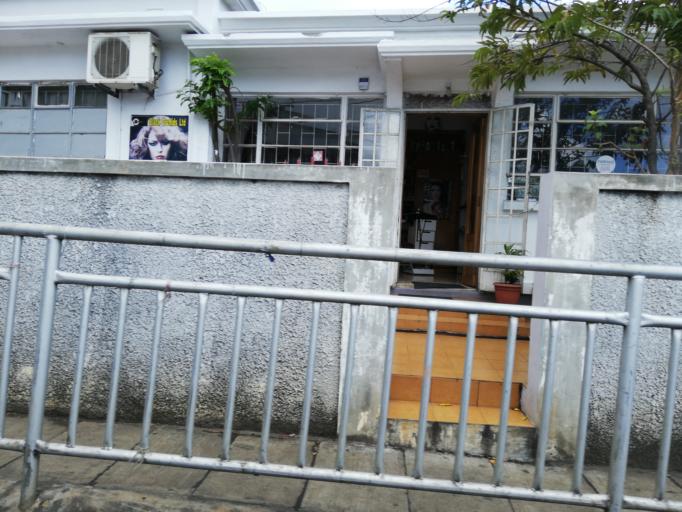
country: MU
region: Pamplemousses
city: Triolet
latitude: -20.0586
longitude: 57.5519
